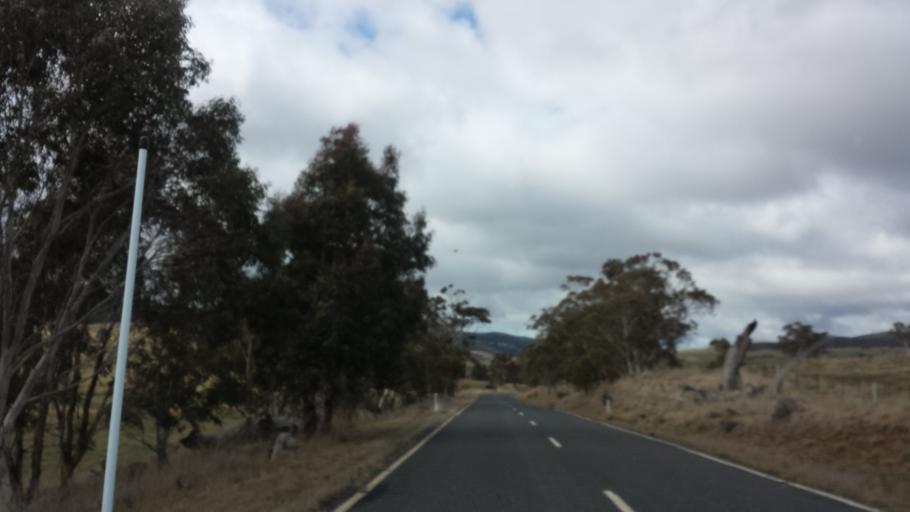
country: AU
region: Victoria
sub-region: Alpine
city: Mount Beauty
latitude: -37.1276
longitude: 147.4584
